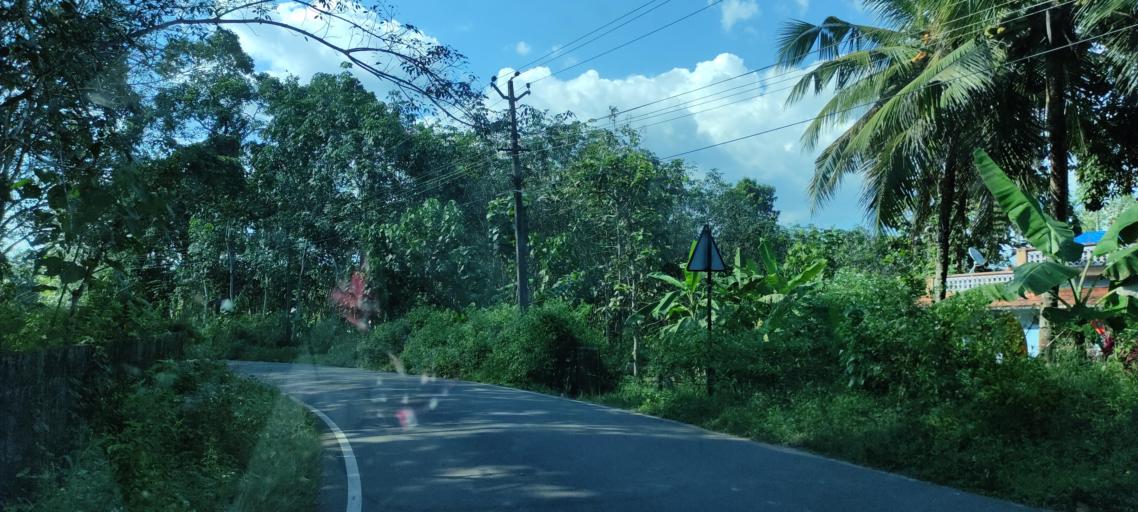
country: IN
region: Kerala
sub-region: Pattanamtitta
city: Adur
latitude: 9.2048
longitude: 76.7485
